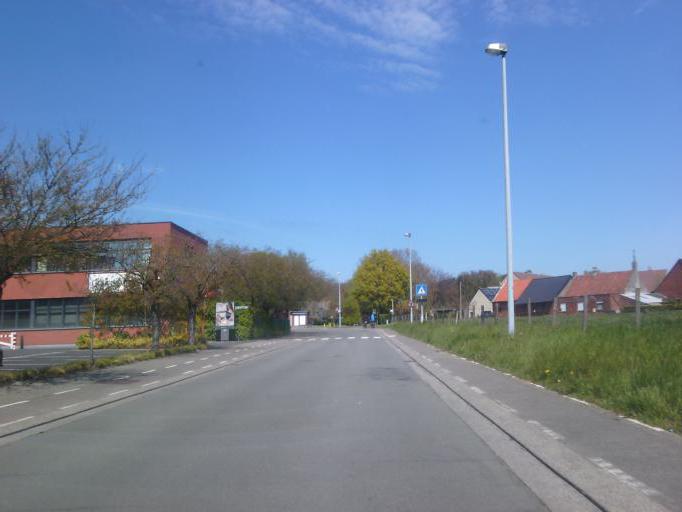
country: BE
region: Flanders
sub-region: Provincie Oost-Vlaanderen
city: Waasmunster
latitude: 51.1476
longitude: 4.0961
